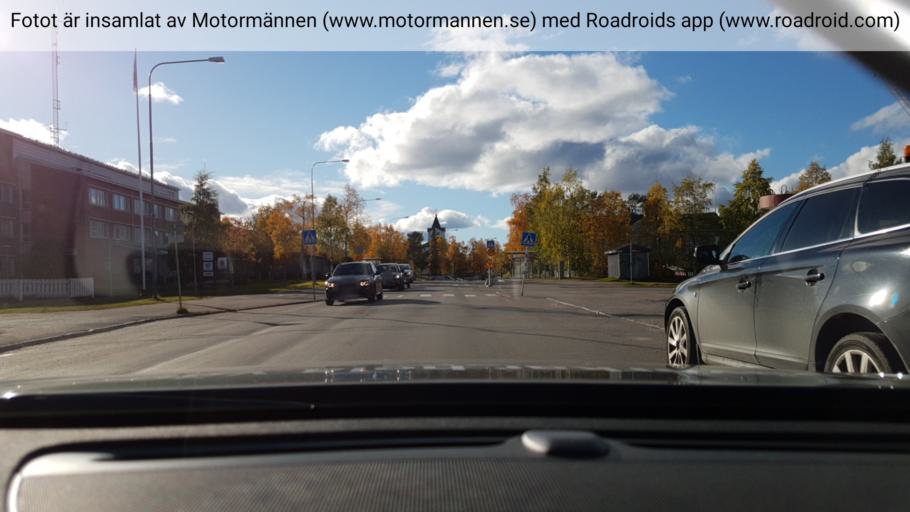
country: SE
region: Norrbotten
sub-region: Gallivare Kommun
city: Gaellivare
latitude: 67.1328
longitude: 20.6657
